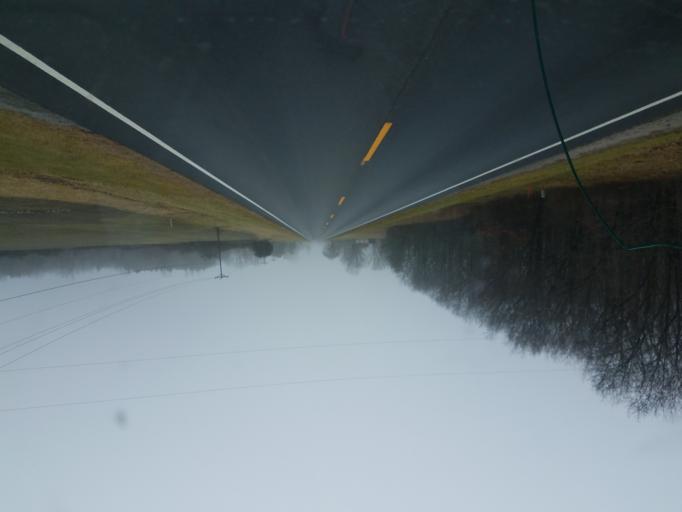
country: US
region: Ohio
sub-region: Champaign County
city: North Lewisburg
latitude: 40.2660
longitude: -83.4787
